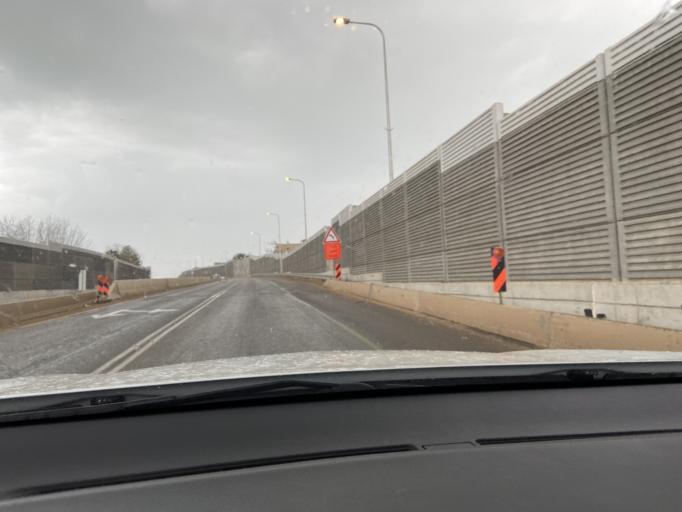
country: IL
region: Northern District
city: El Mazra`a
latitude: 32.9806
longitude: 35.1007
